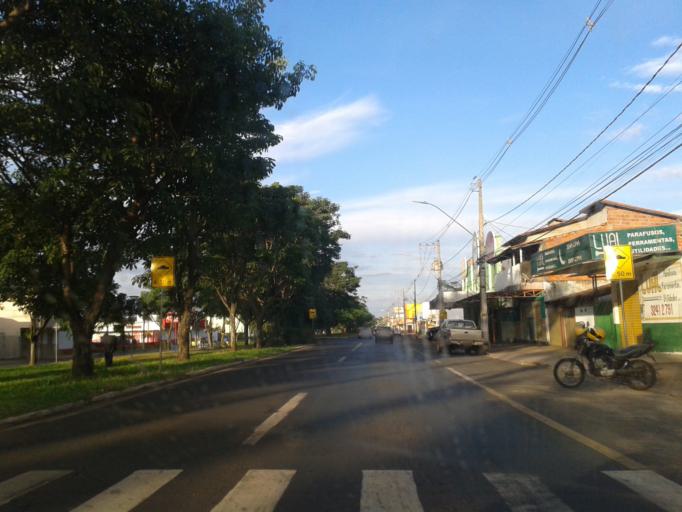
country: BR
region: Minas Gerais
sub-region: Araguari
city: Araguari
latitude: -18.6406
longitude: -48.1821
